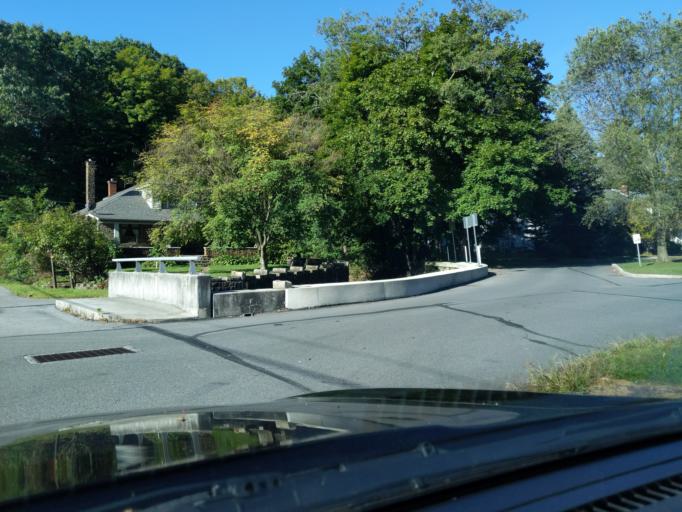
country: US
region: Pennsylvania
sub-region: Blair County
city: Altoona
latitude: 40.5337
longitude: -78.3921
